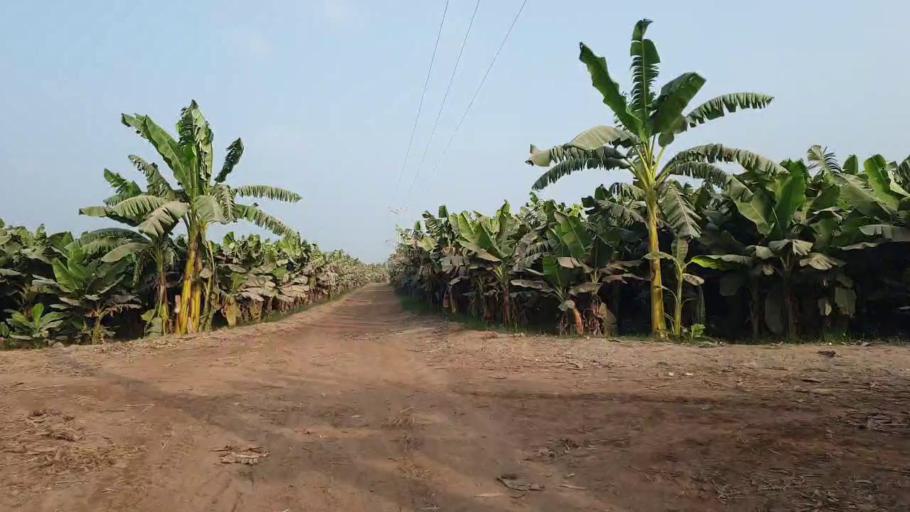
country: PK
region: Sindh
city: Tando Muhammad Khan
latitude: 25.1584
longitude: 68.5851
